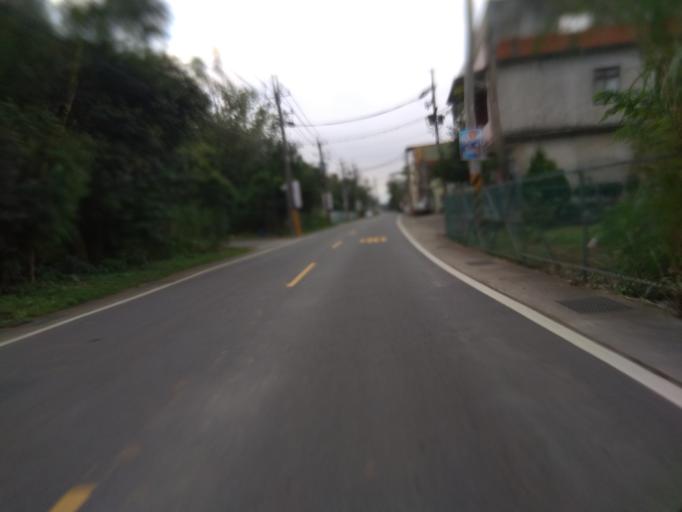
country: TW
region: Taiwan
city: Daxi
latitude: 24.8390
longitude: 121.2072
